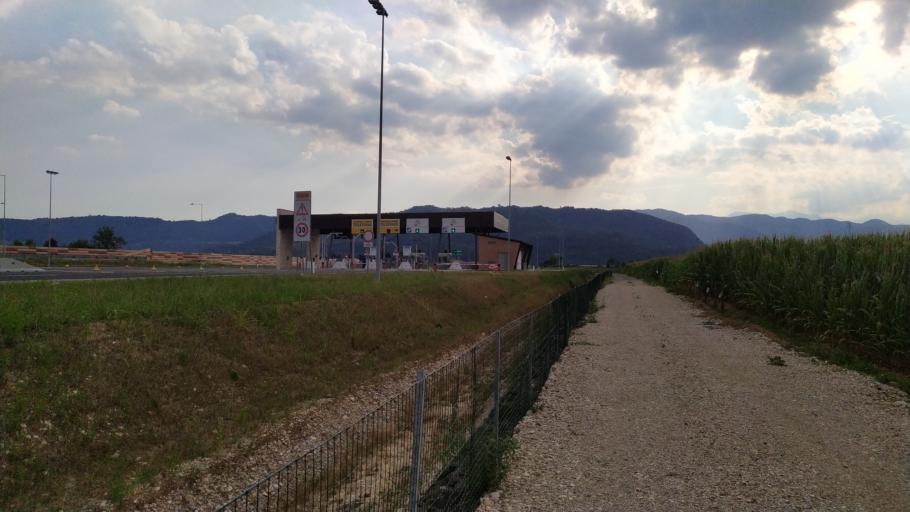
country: IT
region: Veneto
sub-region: Provincia di Vicenza
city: Isola Vicentina
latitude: 45.6498
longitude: 11.4445
